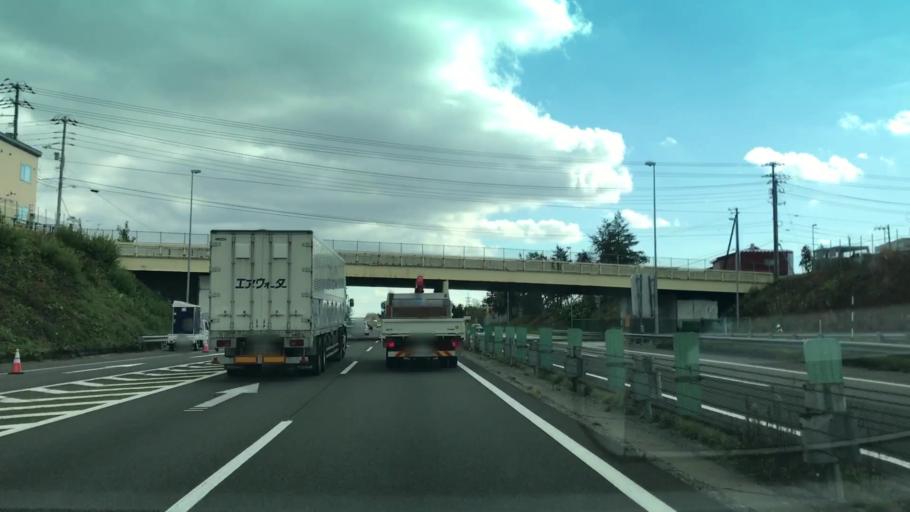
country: JP
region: Hokkaido
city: Kitahiroshima
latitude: 42.9762
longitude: 141.4792
